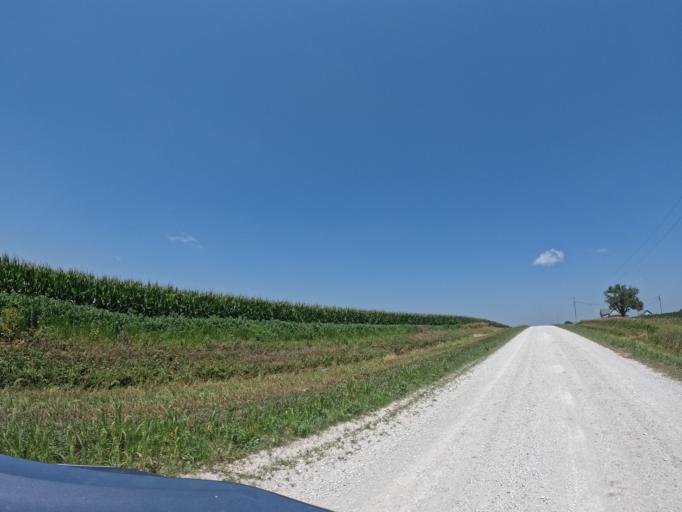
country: US
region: Iowa
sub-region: Keokuk County
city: Sigourney
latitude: 41.2636
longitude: -92.1699
